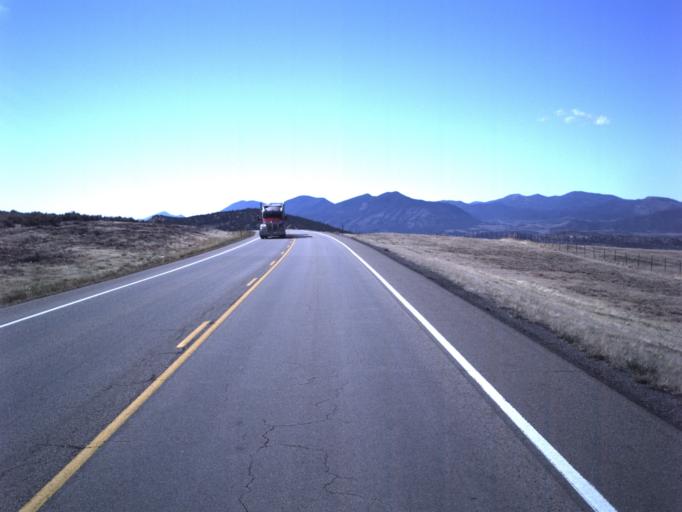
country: US
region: Utah
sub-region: Sanpete County
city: Gunnison
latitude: 39.4060
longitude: -111.9272
